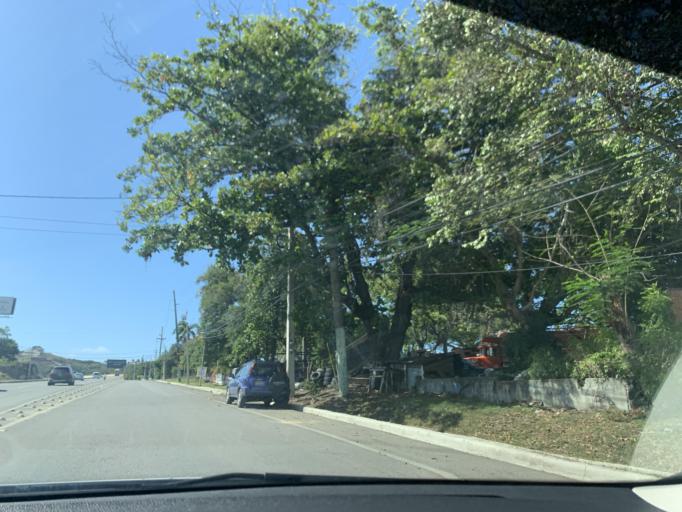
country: DO
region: Puerto Plata
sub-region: Puerto Plata
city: Puerto Plata
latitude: 19.8136
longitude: -70.7314
